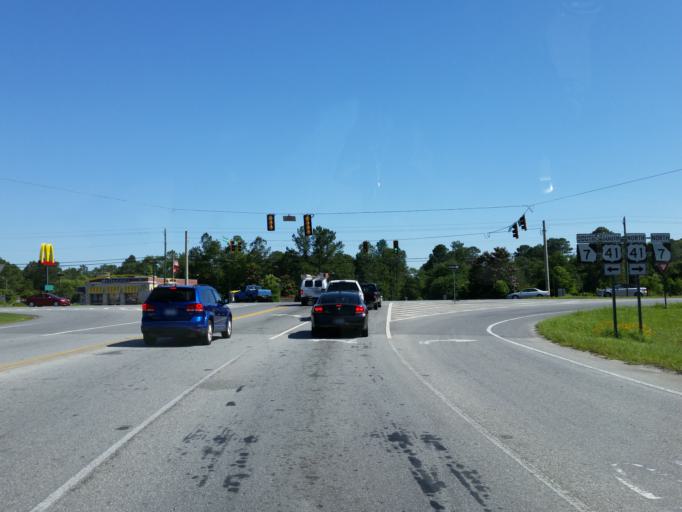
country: US
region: Georgia
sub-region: Lowndes County
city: Remerton
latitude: 30.8977
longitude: -83.3318
